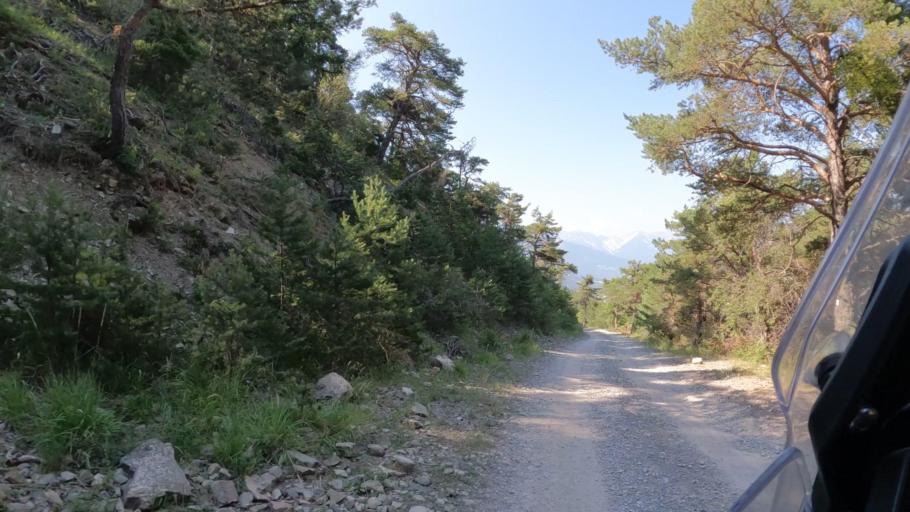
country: FR
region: Provence-Alpes-Cote d'Azur
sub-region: Departement des Hautes-Alpes
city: Embrun
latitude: 44.5878
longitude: 6.5536
